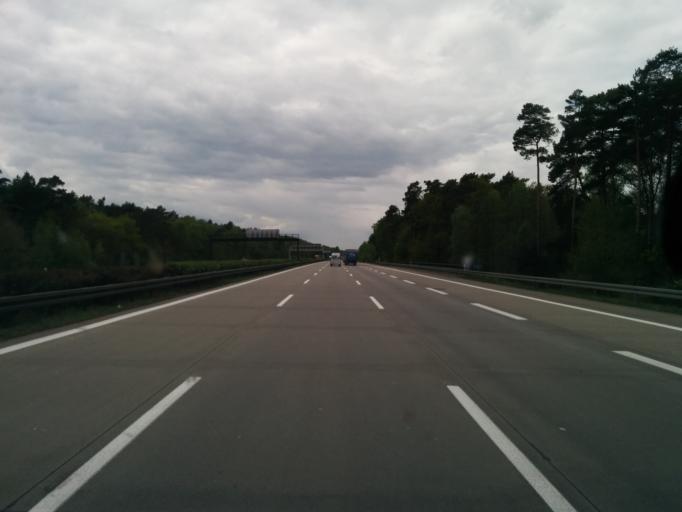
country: DE
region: Brandenburg
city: Gross Kreutz
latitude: 52.3387
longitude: 12.7958
